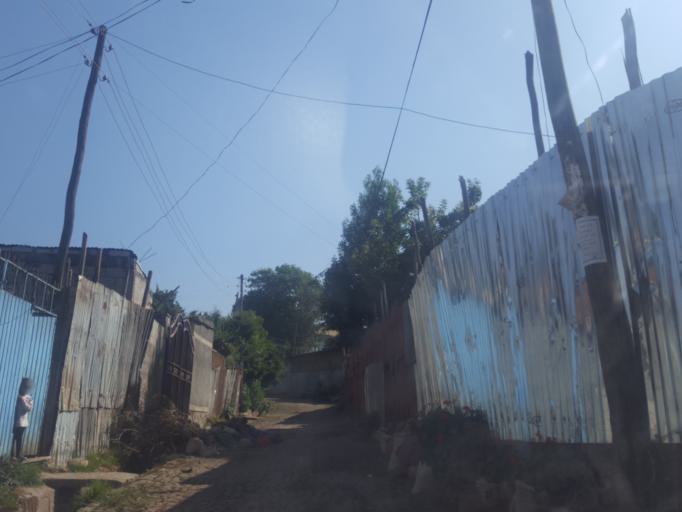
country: ET
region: Adis Abeba
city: Addis Ababa
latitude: 9.0583
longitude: 38.7229
